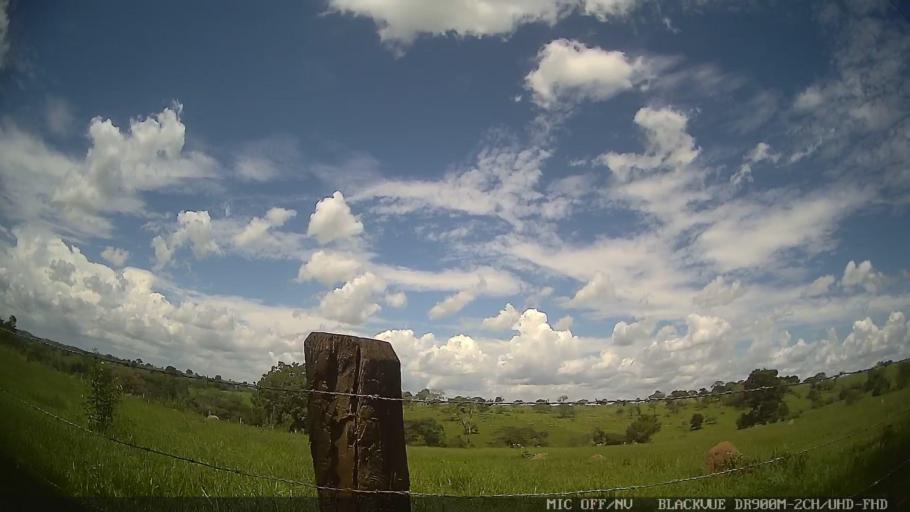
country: BR
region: Sao Paulo
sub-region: Conchas
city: Conchas
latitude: -23.0442
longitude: -47.9938
